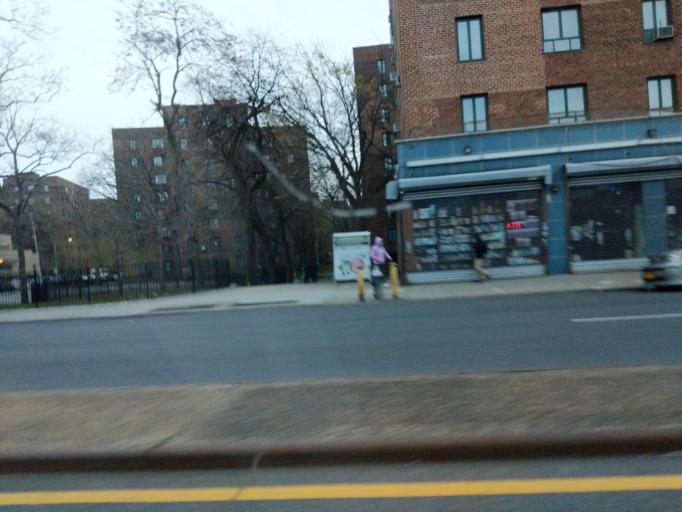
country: US
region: New York
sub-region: Bronx
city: The Bronx
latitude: 40.8423
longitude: -73.8556
